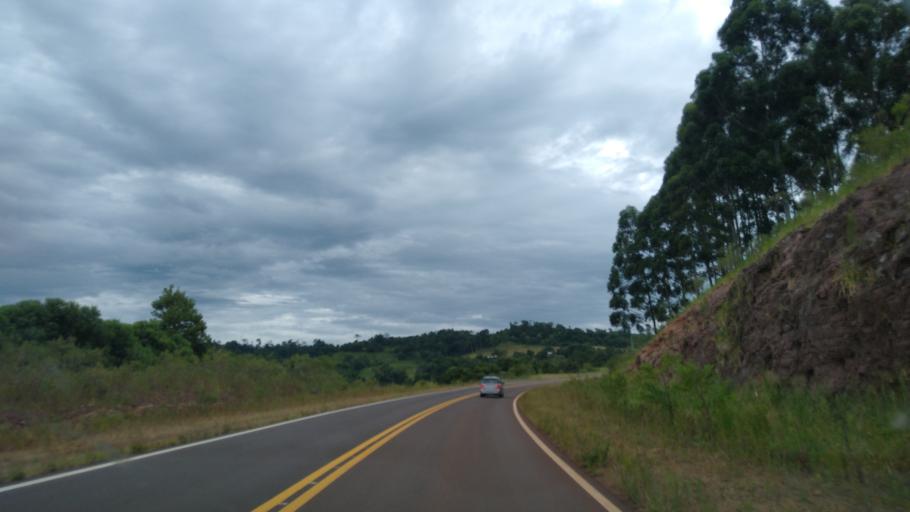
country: AR
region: Misiones
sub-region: Departamento de San Pedro
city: San Pedro
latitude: -26.4563
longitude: -53.8710
